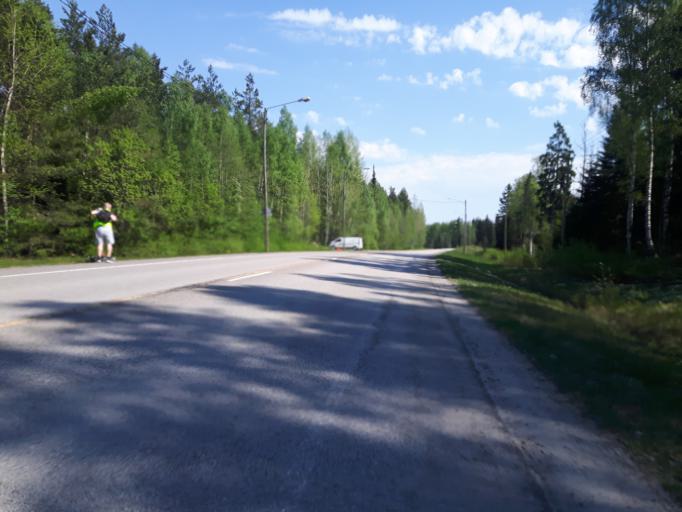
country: FI
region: Uusimaa
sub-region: Porvoo
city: Porvoo
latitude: 60.3708
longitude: 25.5706
